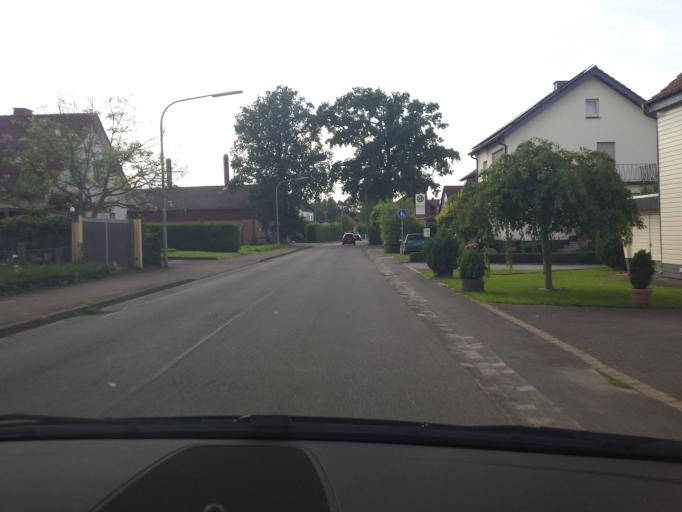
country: DE
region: North Rhine-Westphalia
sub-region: Regierungsbezirk Arnsberg
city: Lippstadt
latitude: 51.6541
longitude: 8.2829
